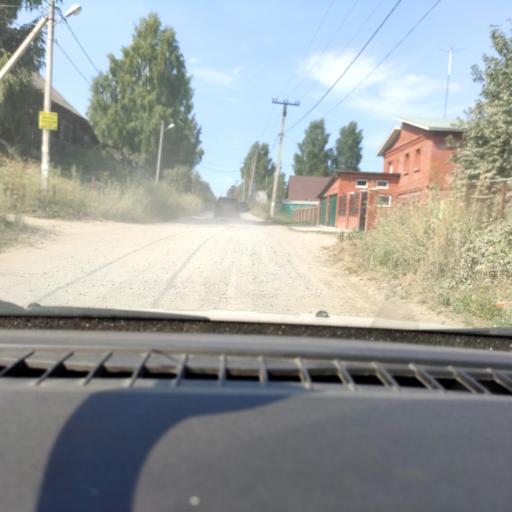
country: RU
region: Perm
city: Polazna
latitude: 58.1379
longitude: 56.4574
